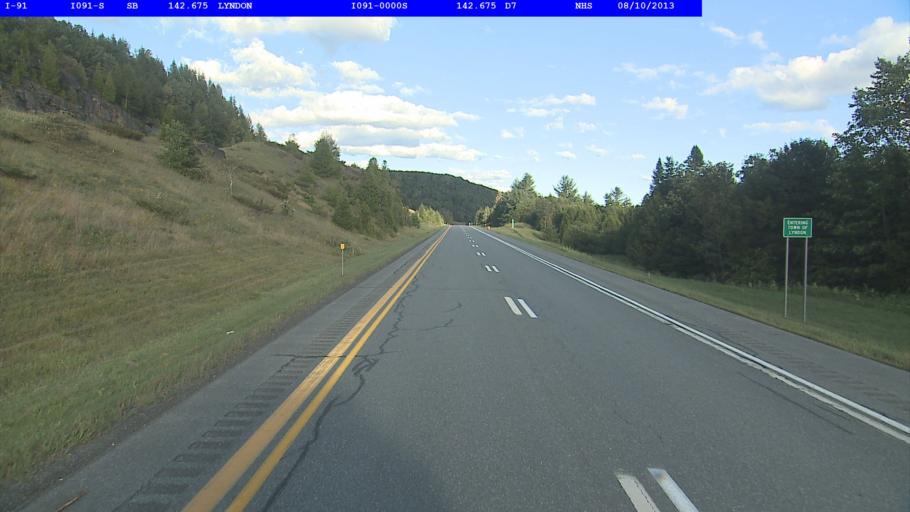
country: US
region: Vermont
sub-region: Caledonia County
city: Lyndonville
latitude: 44.5819
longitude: -72.0613
